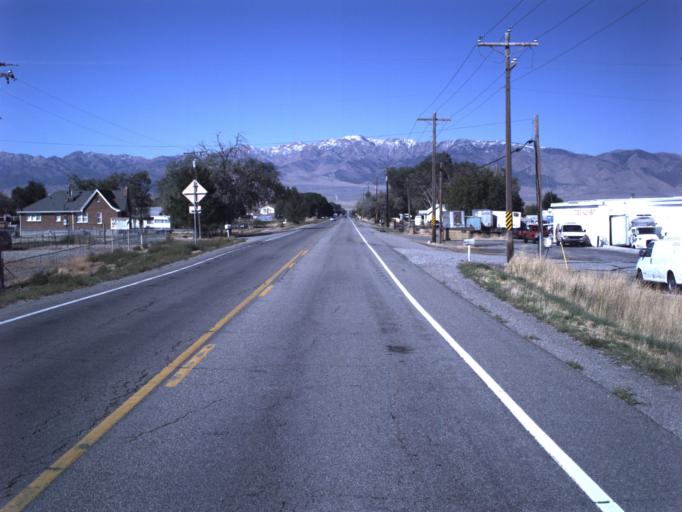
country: US
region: Utah
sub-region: Tooele County
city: Grantsville
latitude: 40.5996
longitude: -112.4159
